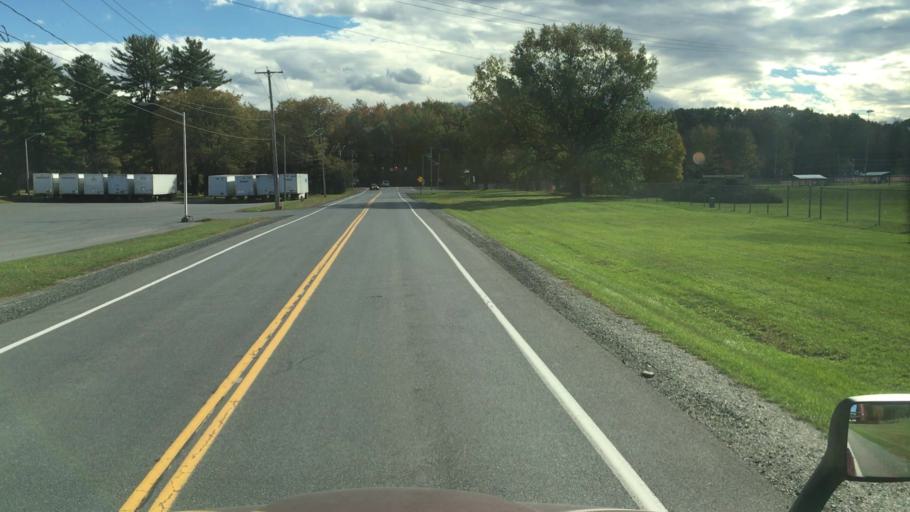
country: US
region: New York
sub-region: Saratoga County
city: Milton
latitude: 43.0620
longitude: -73.8221
